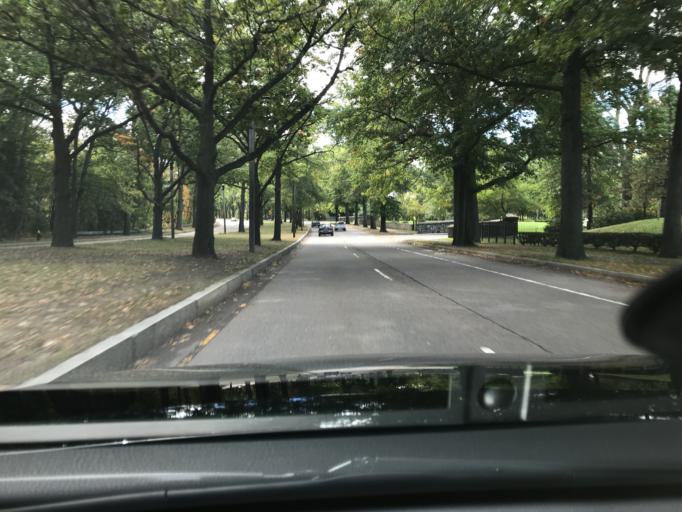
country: US
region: Massachusetts
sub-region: Norfolk County
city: Dedham
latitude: 42.2862
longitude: -71.1723
